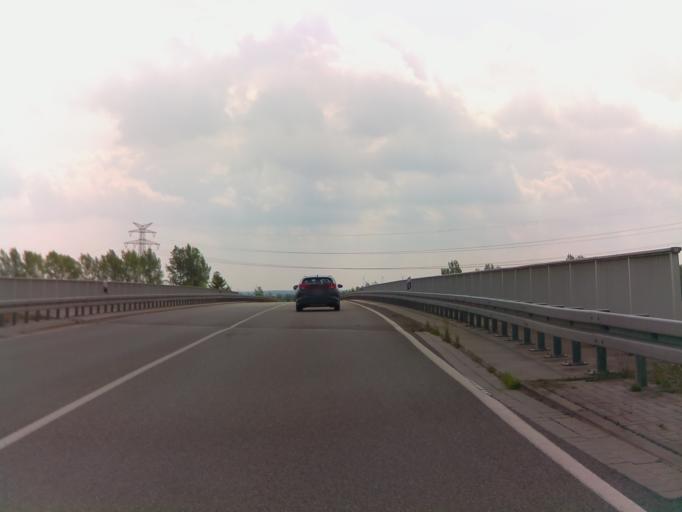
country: DE
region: Saxony-Anhalt
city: Luderitz
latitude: 52.5732
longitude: 11.6915
